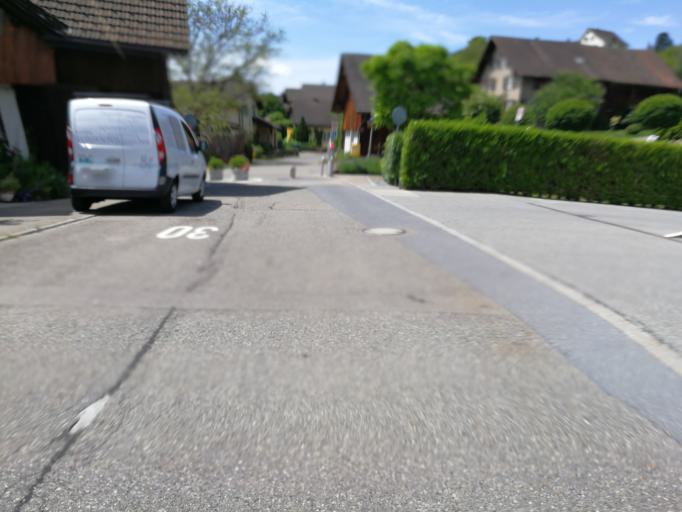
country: CH
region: Saint Gallen
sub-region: Wahlkreis See-Gaster
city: Rapperswil
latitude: 47.2399
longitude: 8.8167
